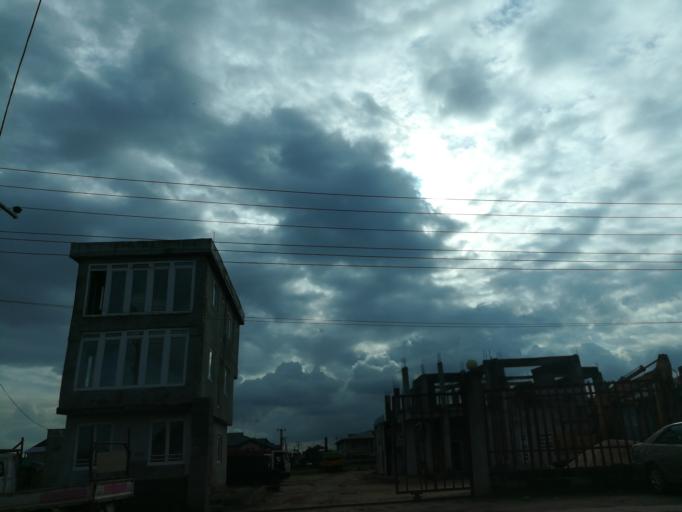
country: NG
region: Lagos
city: Ebute Ikorodu
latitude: 6.6086
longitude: 3.4844
